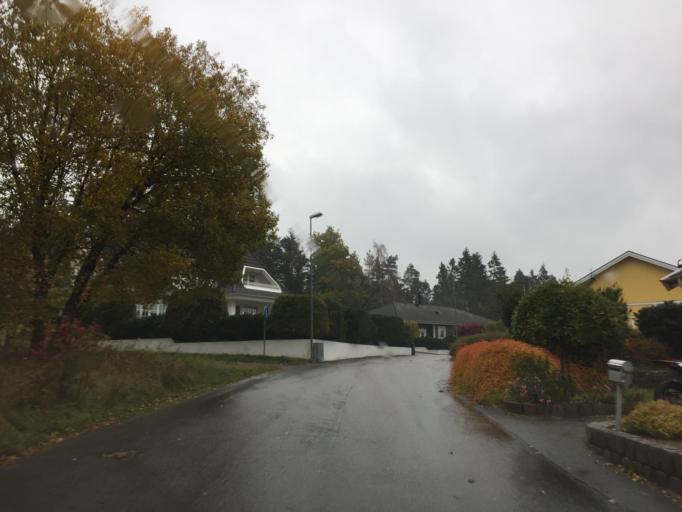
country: SE
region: Vaestra Goetaland
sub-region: Trollhattan
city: Trollhattan
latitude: 58.3241
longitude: 12.2774
